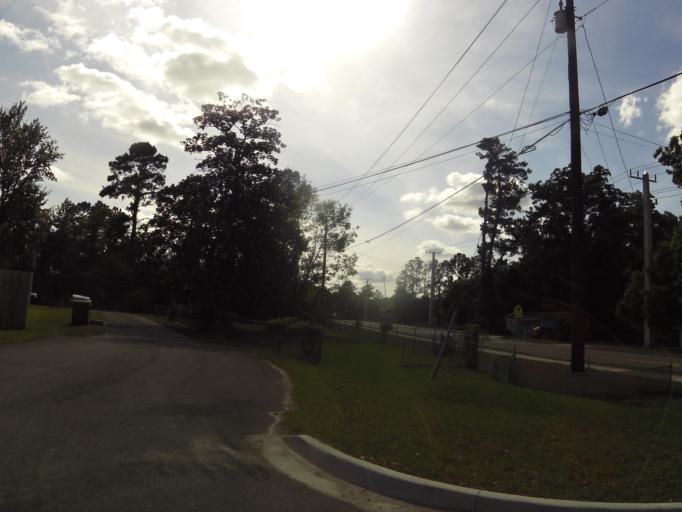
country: US
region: Florida
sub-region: Nassau County
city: Callahan
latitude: 30.5706
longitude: -81.8373
